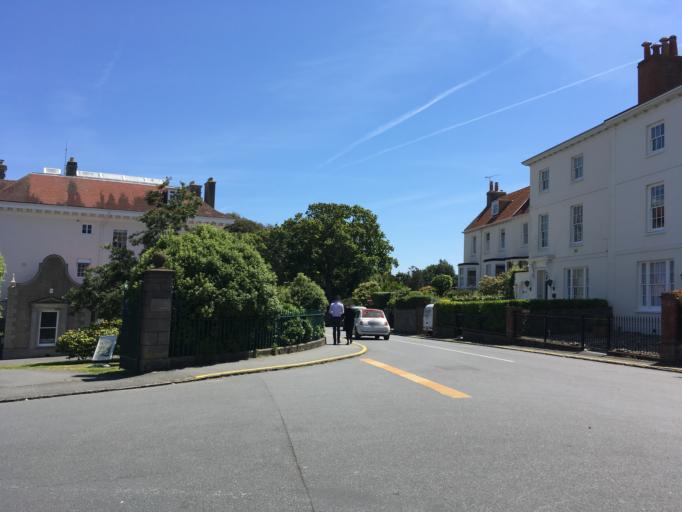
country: GG
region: St Peter Port
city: Saint Peter Port
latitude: 49.4593
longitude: -2.5427
